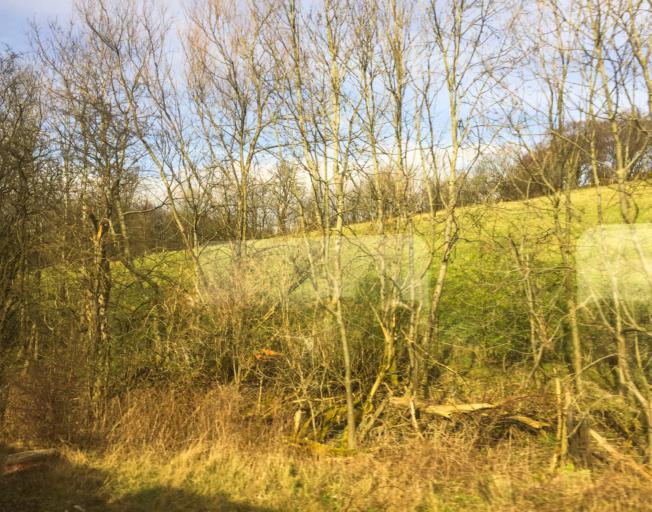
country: GB
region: Scotland
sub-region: East Dunbartonshire
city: Bearsden
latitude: 55.8954
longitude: -4.3190
